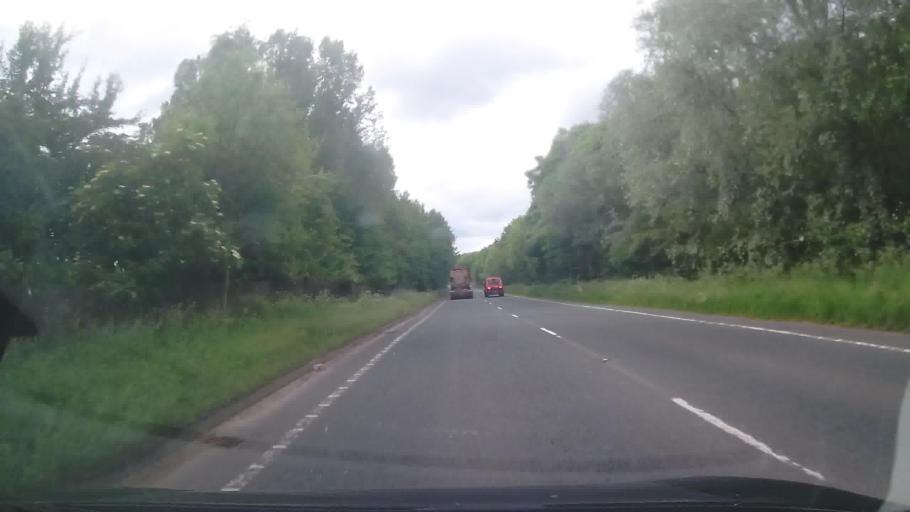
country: GB
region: England
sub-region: Telford and Wrekin
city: Newport
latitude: 52.7751
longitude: -2.3664
